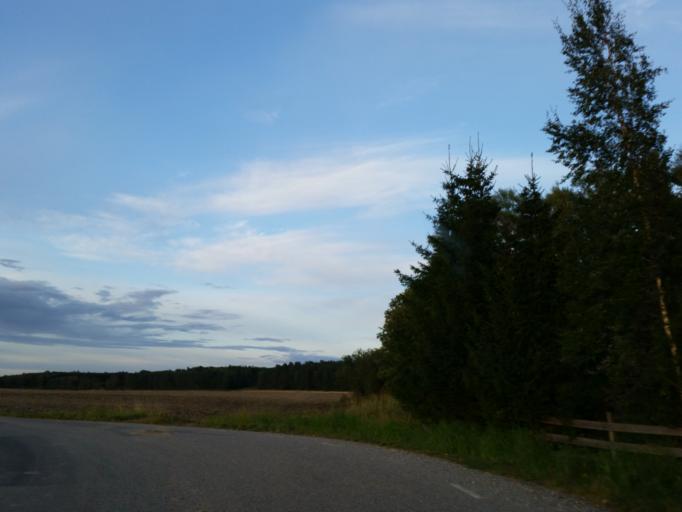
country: SE
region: Stockholm
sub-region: Sigtuna Kommun
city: Marsta
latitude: 59.6345
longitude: 17.8808
